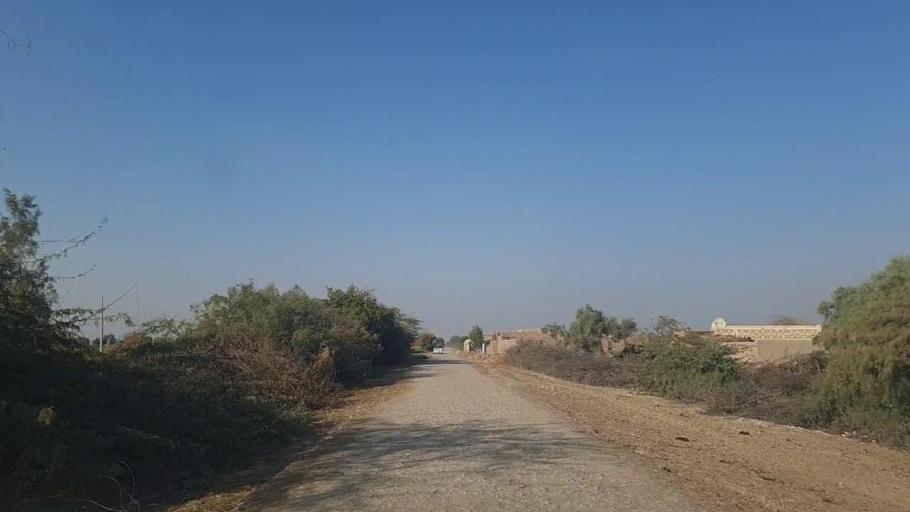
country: PK
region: Sindh
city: Jam Sahib
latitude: 26.3191
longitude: 68.7147
